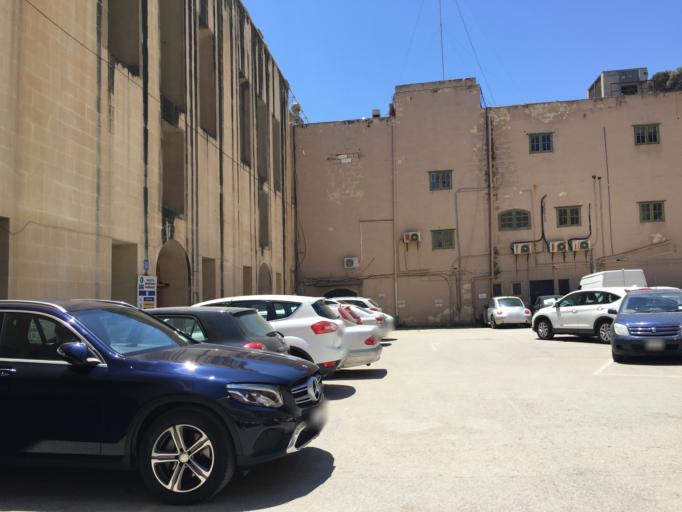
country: MT
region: Il-Furjana
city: Floriana
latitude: 35.8900
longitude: 14.5077
